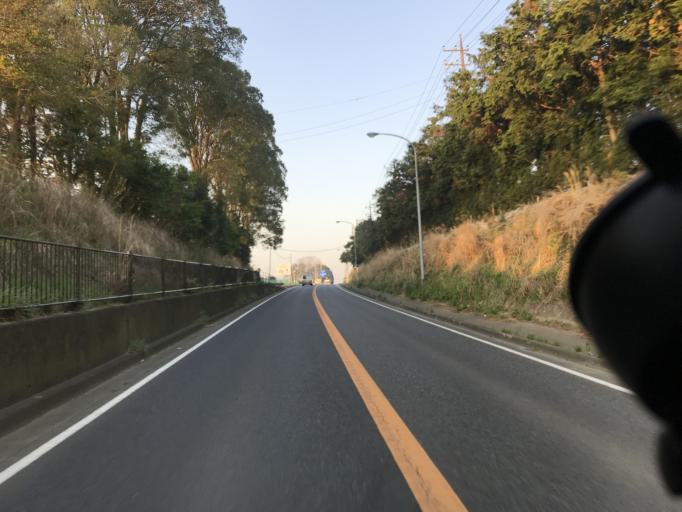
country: JP
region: Chiba
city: Narita
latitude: 35.8111
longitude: 140.3872
